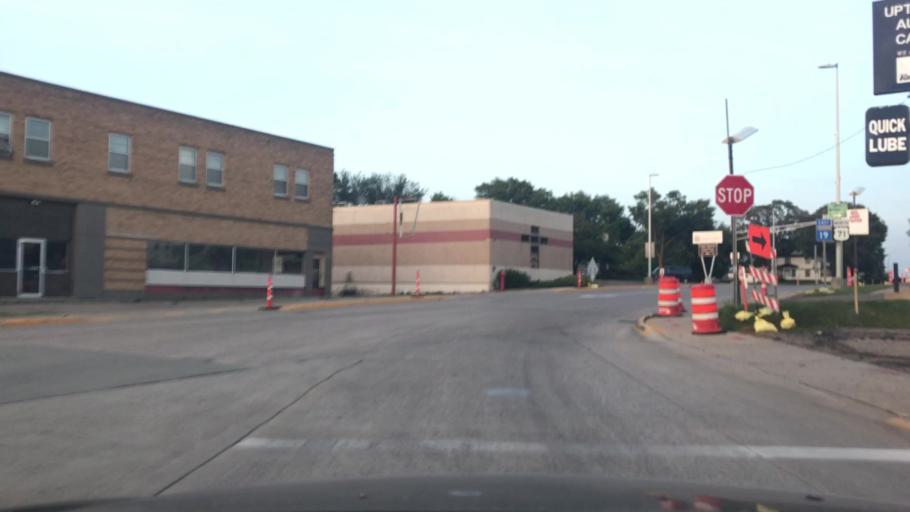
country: US
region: Minnesota
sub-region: Redwood County
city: Redwood Falls
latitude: 44.5412
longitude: -95.1187
